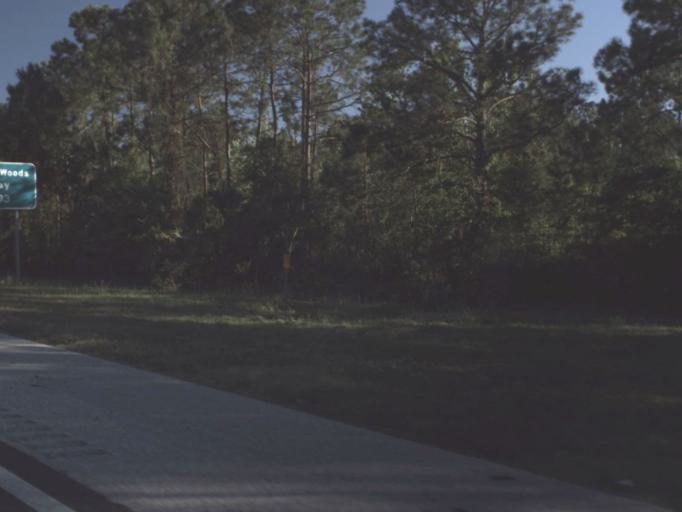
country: US
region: Florida
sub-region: Flagler County
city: Palm Coast
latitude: 29.6141
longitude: -81.2561
